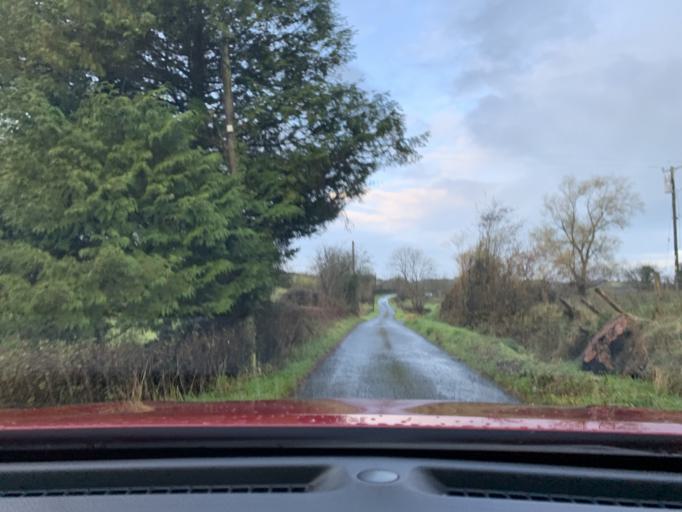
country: IE
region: Connaught
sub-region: Sligo
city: Ballymote
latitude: 54.0466
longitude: -8.5357
